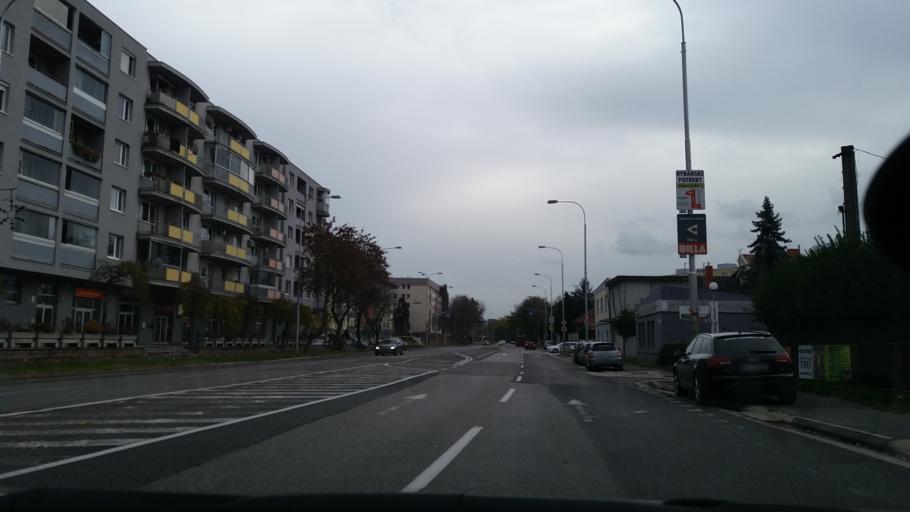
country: SK
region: Bratislavsky
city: Bratislava
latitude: 48.1281
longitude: 17.0940
